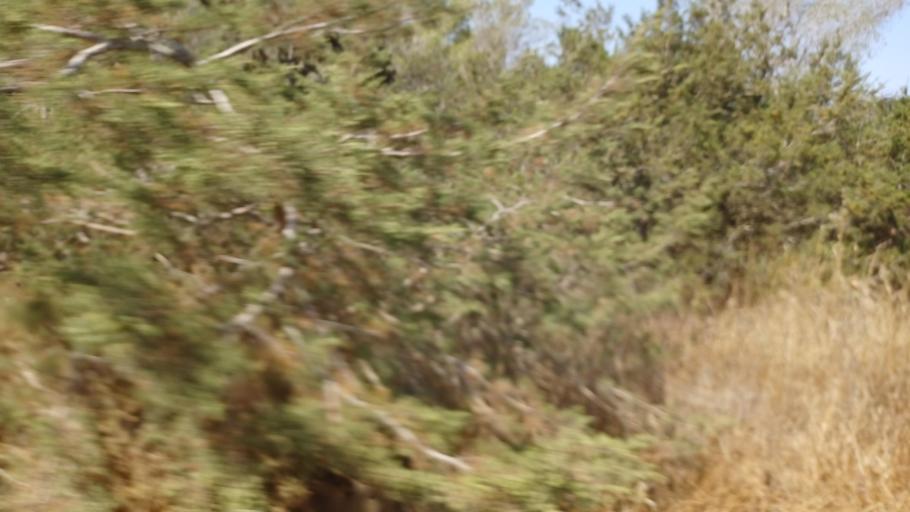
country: CY
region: Ammochostos
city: Paralimni
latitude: 35.0042
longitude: 33.9595
